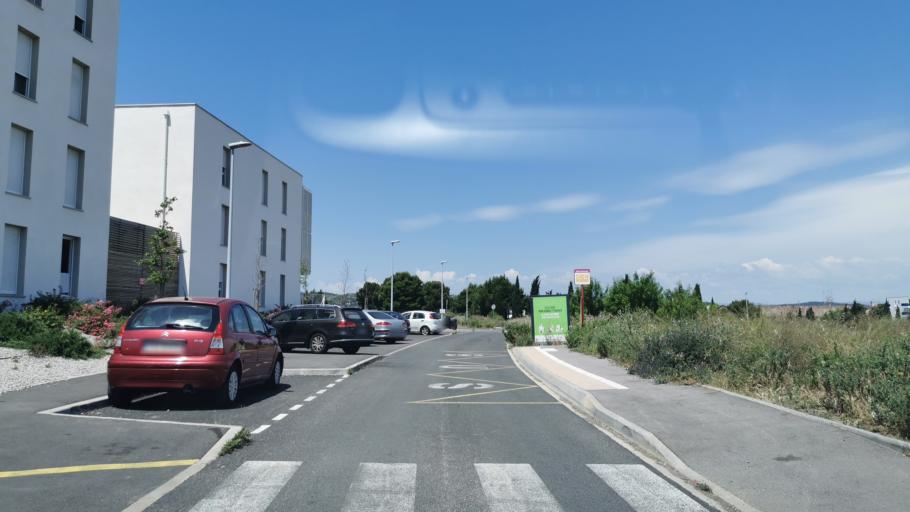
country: FR
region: Languedoc-Roussillon
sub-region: Departement de l'Aude
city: Narbonne
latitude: 43.1658
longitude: 2.9933
